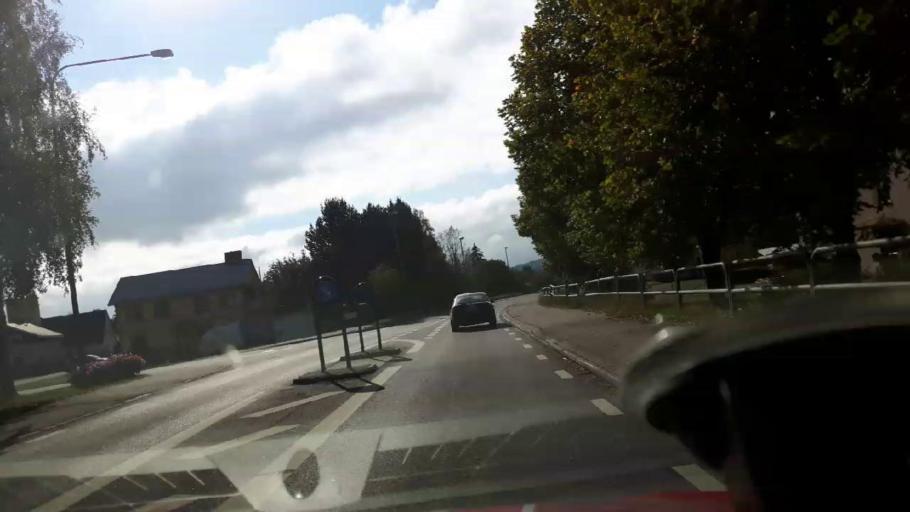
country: SE
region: Gaevleborg
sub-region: Bollnas Kommun
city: Arbra
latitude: 61.5170
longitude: 16.3634
